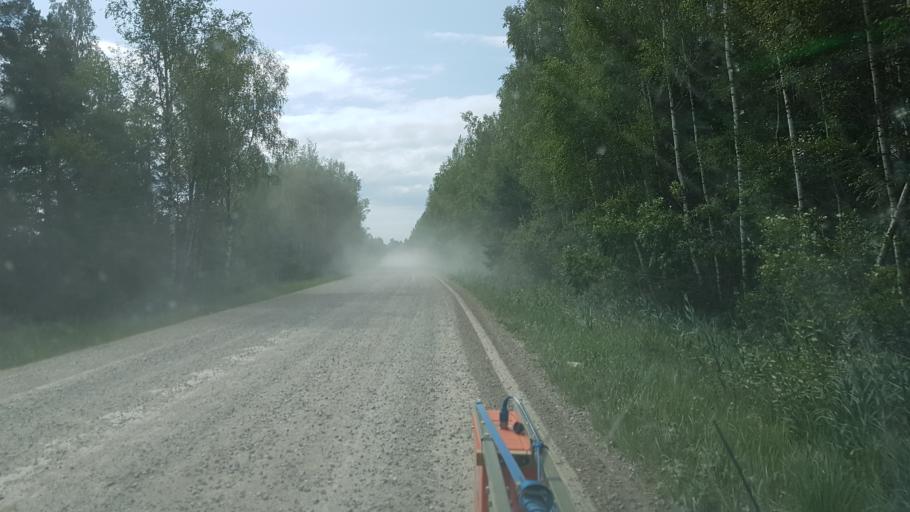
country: EE
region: Paernumaa
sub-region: Audru vald
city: Audru
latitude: 58.5202
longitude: 24.4053
